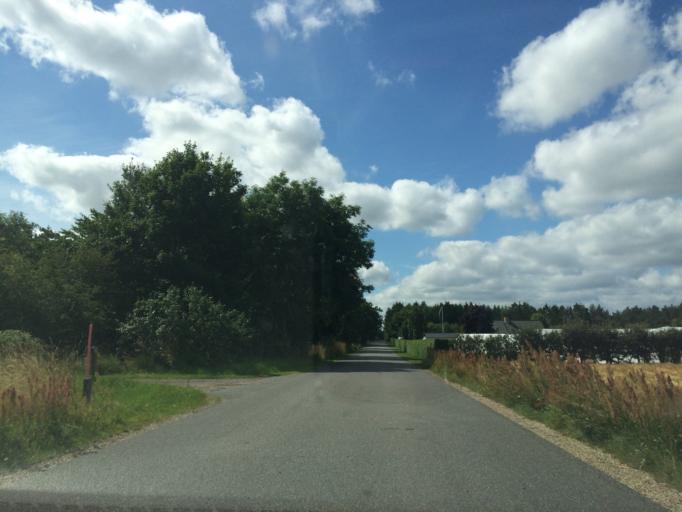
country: DK
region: Central Jutland
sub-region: Silkeborg Kommune
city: Svejbaek
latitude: 56.2013
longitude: 9.6707
